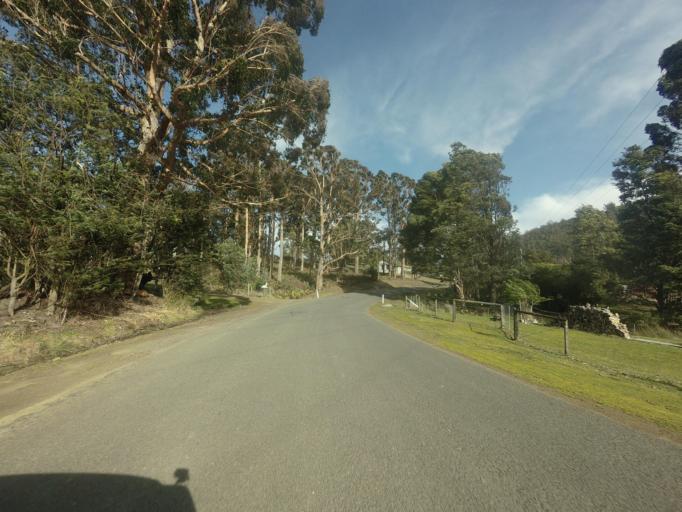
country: AU
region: Tasmania
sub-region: Huon Valley
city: Huonville
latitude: -43.0466
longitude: 147.1148
